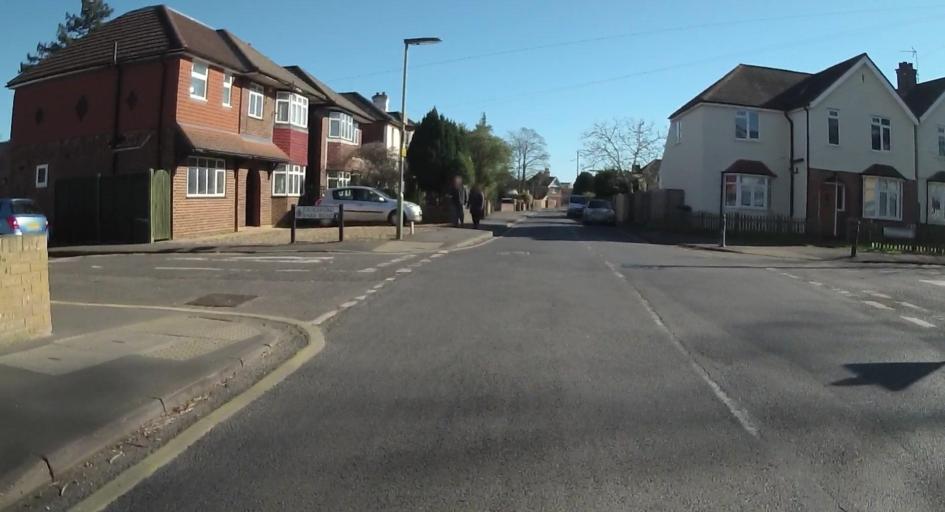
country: GB
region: England
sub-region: Surrey
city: Addlestone
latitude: 51.3715
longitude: -0.4845
